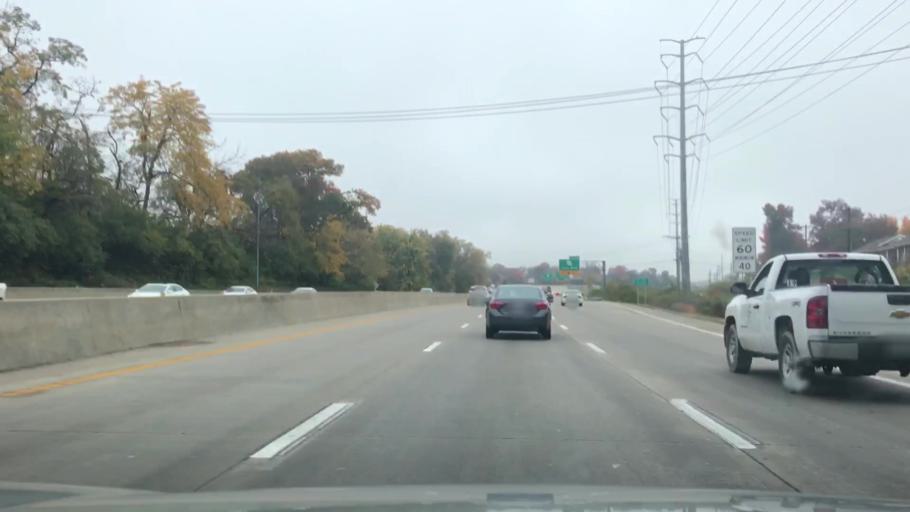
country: US
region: Missouri
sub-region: Saint Louis County
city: Olivette
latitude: 38.6681
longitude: -90.3612
